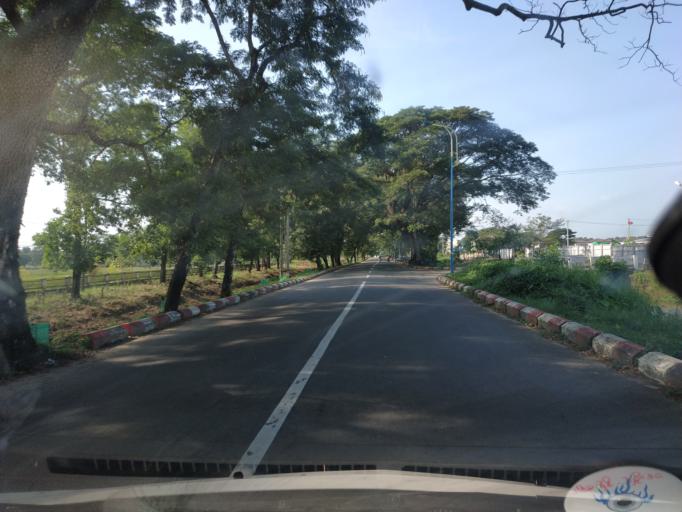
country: MM
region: Ayeyarwady
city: Pathein
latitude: 16.8083
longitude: 94.7564
